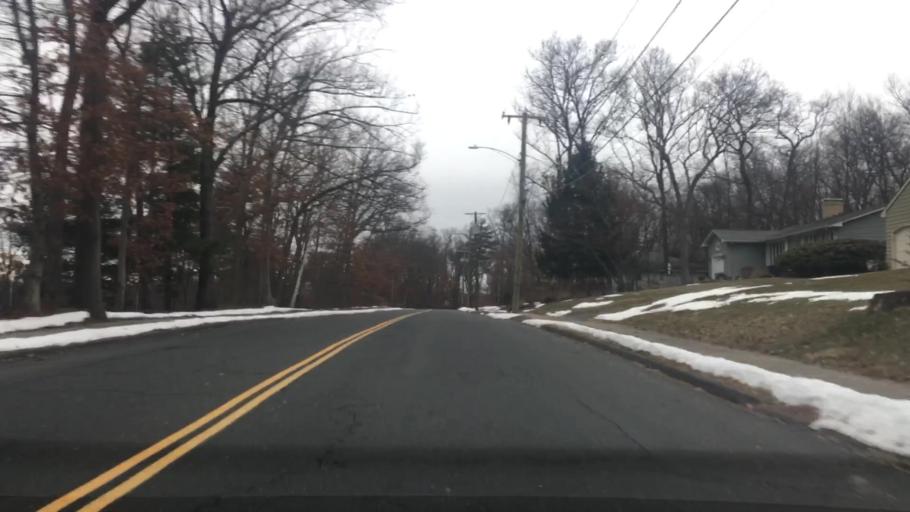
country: US
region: Connecticut
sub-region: Hartford County
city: Bristol
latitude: 41.6855
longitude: -72.9190
